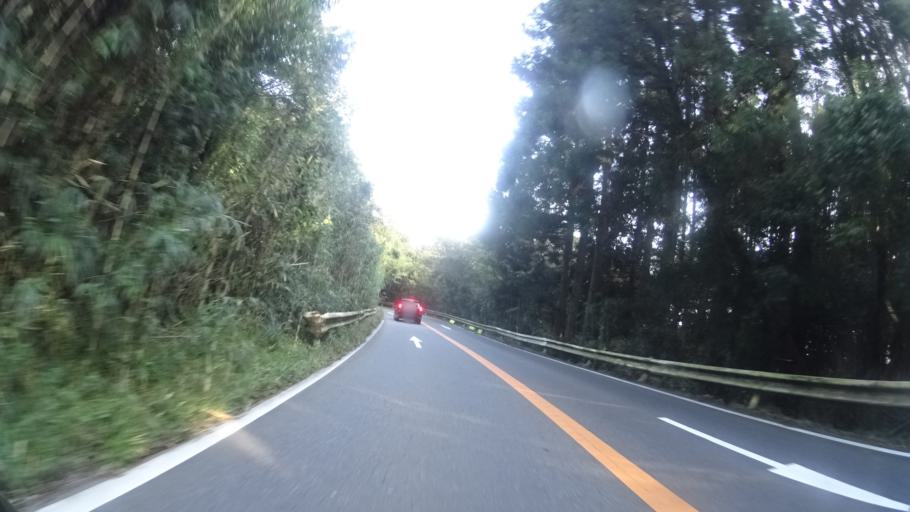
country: JP
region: Oita
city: Beppu
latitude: 33.2693
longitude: 131.4362
